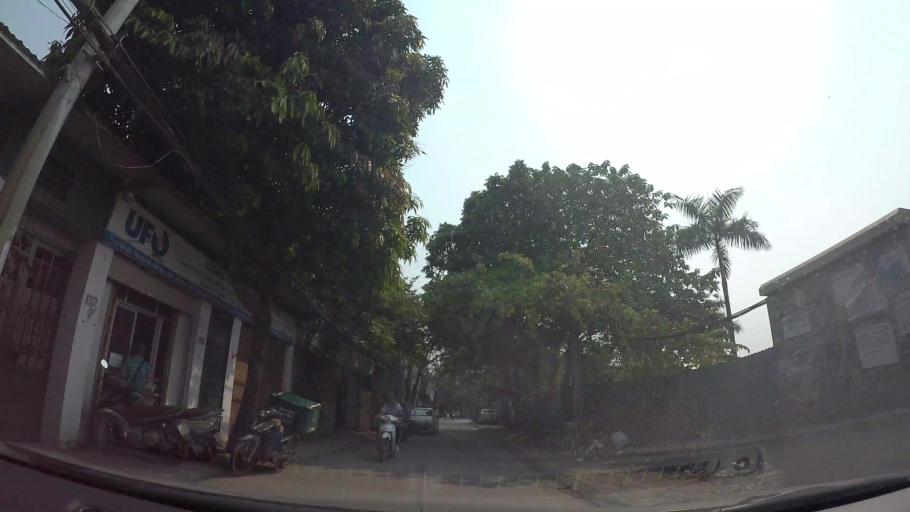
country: VN
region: Ha Noi
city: Thanh Xuan
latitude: 20.9905
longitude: 105.8280
